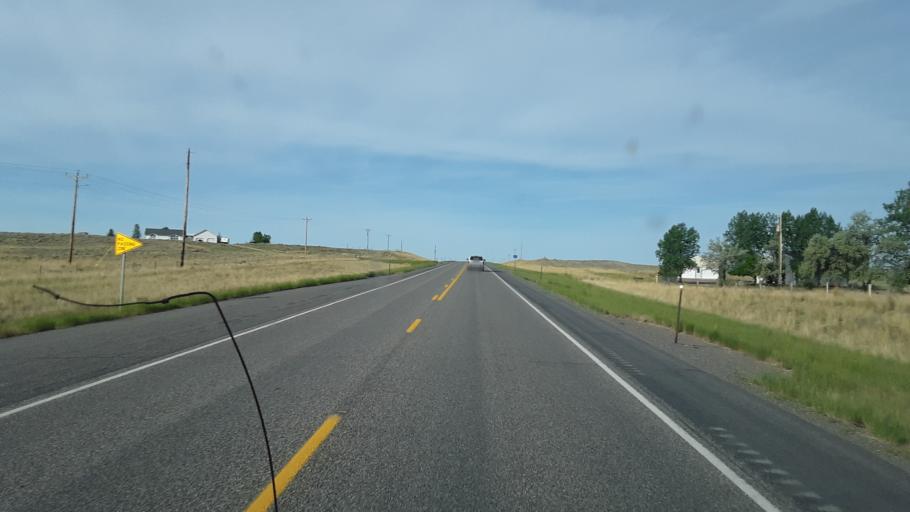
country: US
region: Wyoming
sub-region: Fremont County
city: Riverton
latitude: 43.1645
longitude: -108.2656
